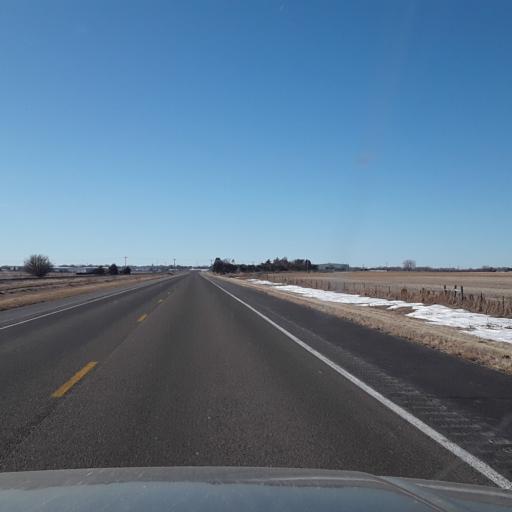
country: US
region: Nebraska
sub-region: Kearney County
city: Minden
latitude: 40.5128
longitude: -98.9202
